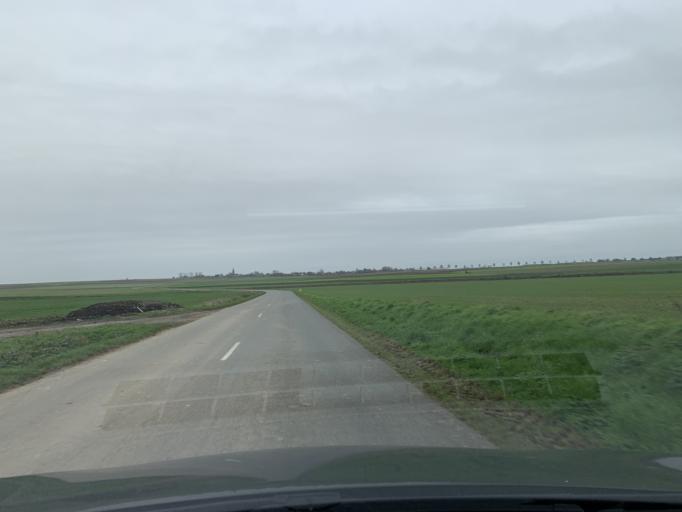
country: FR
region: Nord-Pas-de-Calais
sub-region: Departement du Pas-de-Calais
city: Oisy-le-Verger
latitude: 50.2425
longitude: 3.1389
